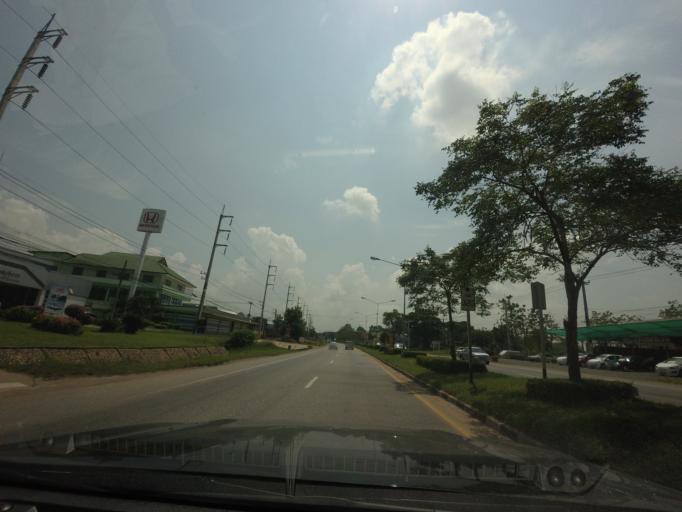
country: TH
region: Uttaradit
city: Uttaradit
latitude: 17.6041
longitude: 100.1237
